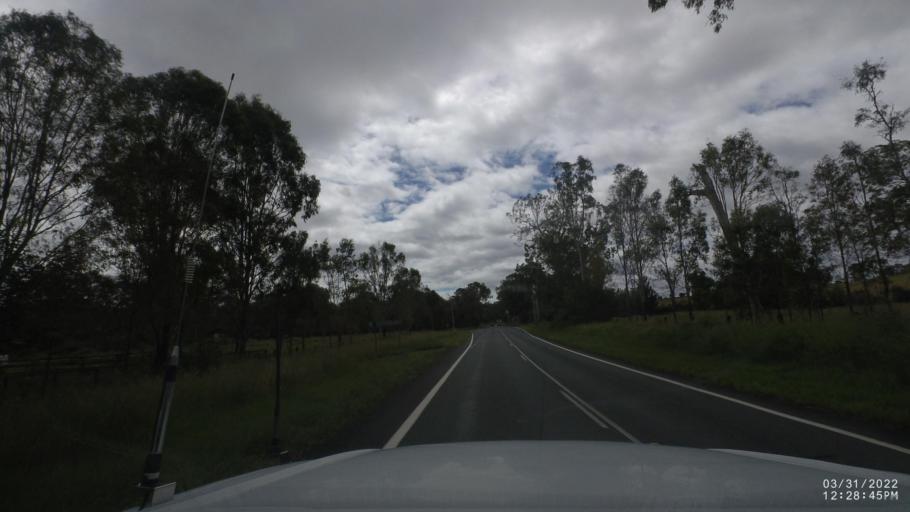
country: AU
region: Queensland
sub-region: Logan
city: Cedar Vale
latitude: -27.9300
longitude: 153.0796
